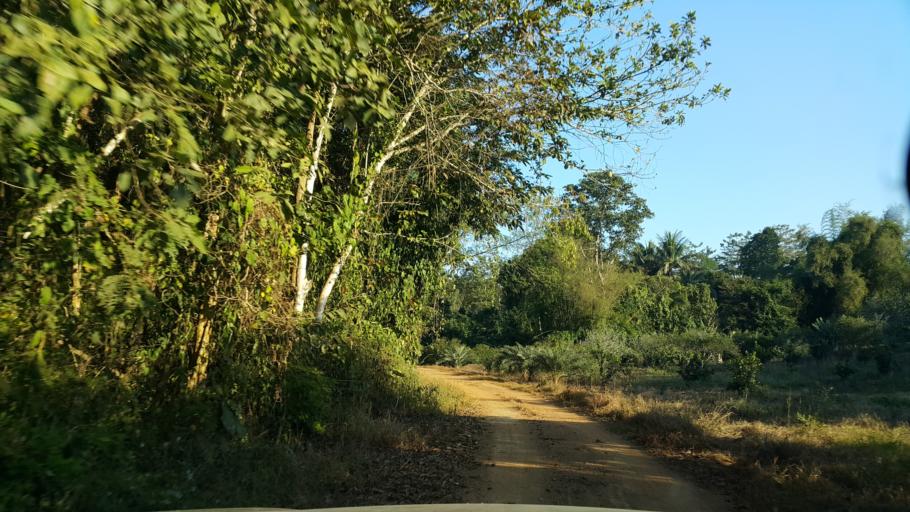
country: TH
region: Sukhothai
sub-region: Amphoe Si Satchanalai
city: Si Satchanalai
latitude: 17.5839
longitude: 99.6077
